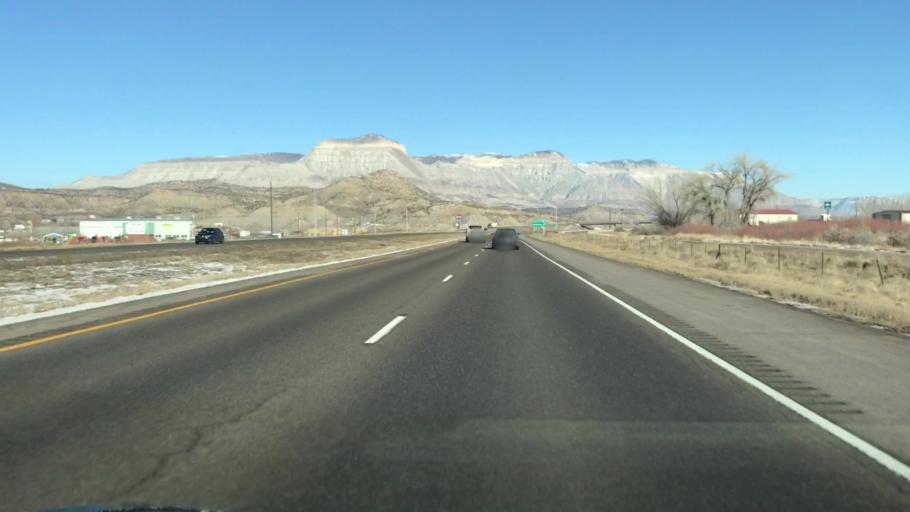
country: US
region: Colorado
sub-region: Garfield County
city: Parachute
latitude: 39.3176
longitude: -108.2113
